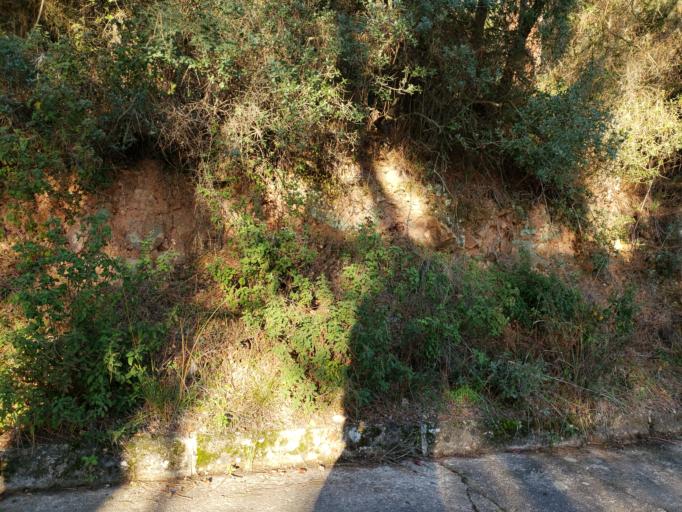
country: TR
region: Istanbul
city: Adalan
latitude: 40.8744
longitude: 29.0893
